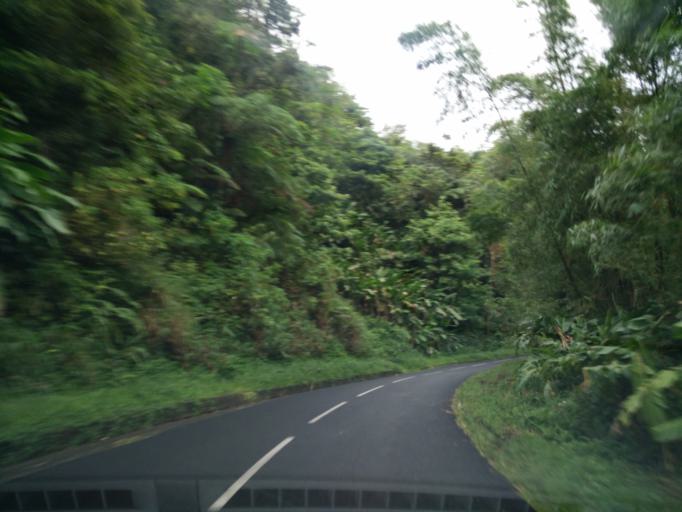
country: MQ
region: Martinique
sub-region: Martinique
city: Le Morne-Rouge
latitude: 14.7252
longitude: -61.1055
